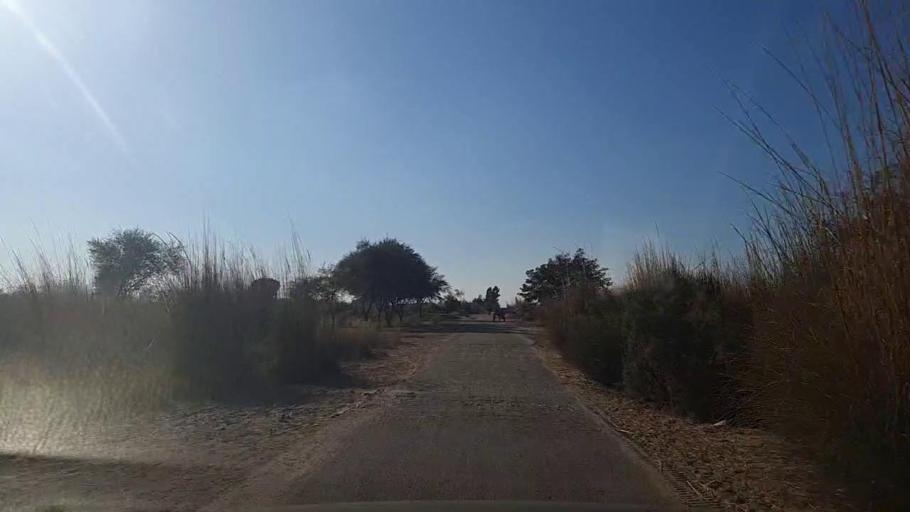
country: PK
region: Sindh
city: Khadro
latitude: 26.2412
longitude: 68.8767
